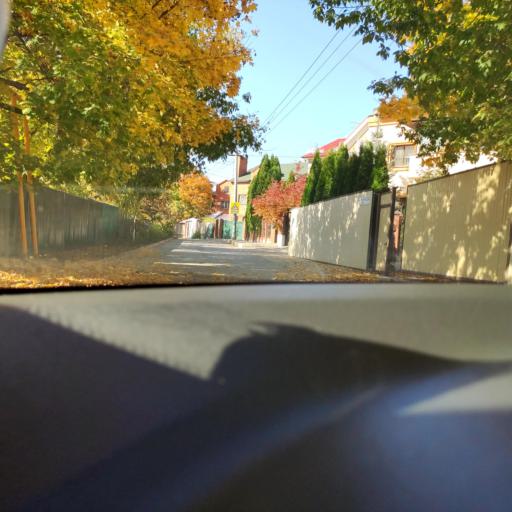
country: RU
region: Samara
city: Samara
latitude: 53.2663
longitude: 50.1908
